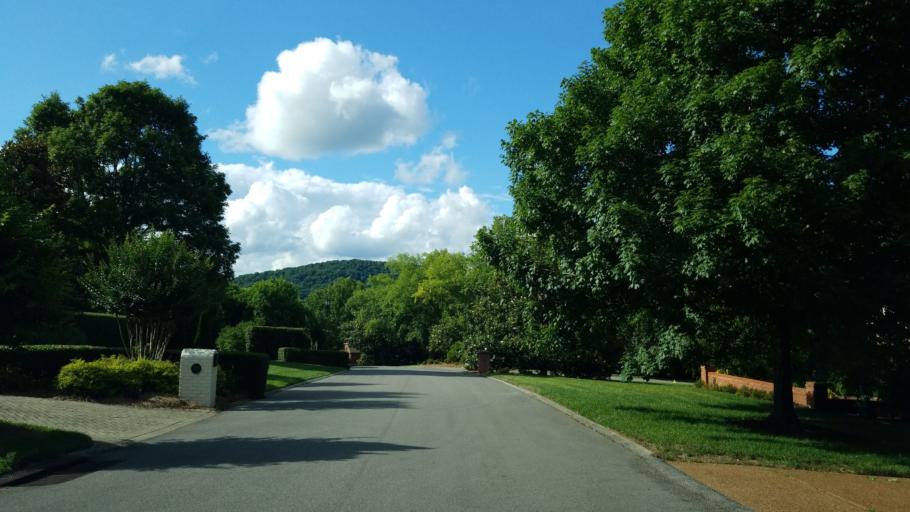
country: US
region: Tennessee
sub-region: Davidson County
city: Forest Hills
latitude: 36.0296
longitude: -86.8348
